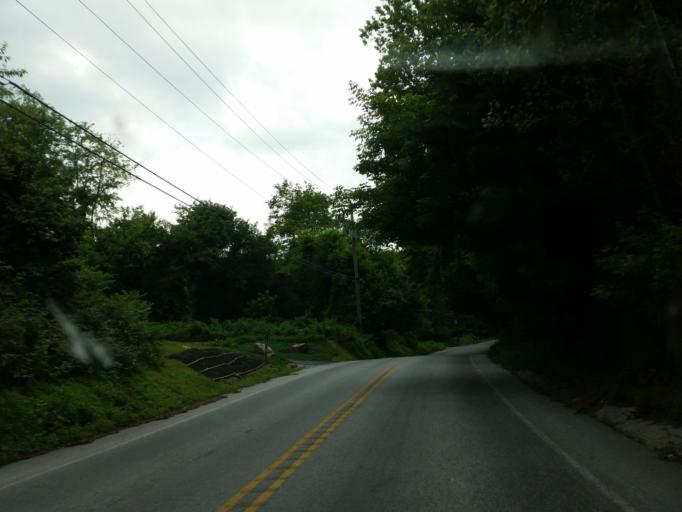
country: US
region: Pennsylvania
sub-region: Chester County
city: Oxford
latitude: 39.8576
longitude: -75.9759
